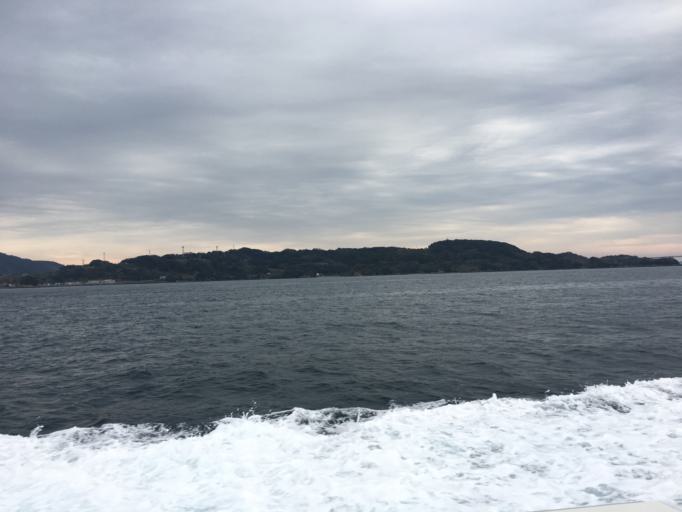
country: JP
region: Nagasaki
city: Nagasaki-shi
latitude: 32.7080
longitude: 129.8028
